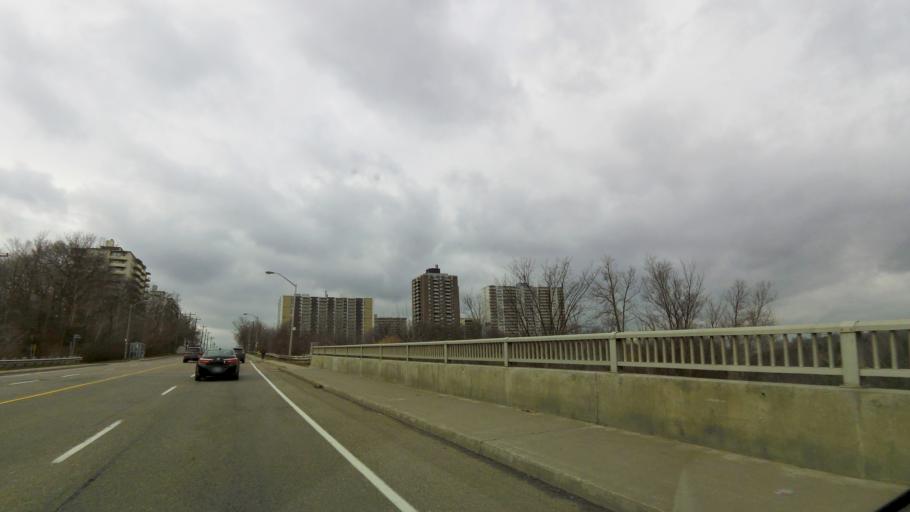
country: CA
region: Ontario
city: North York
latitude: 43.7568
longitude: -79.4317
